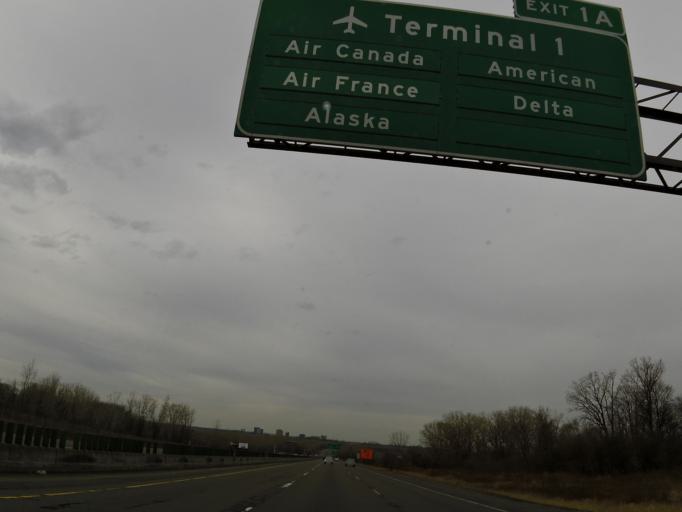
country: US
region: Minnesota
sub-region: Dakota County
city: Mendota Heights
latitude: 44.8613
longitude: -93.1701
